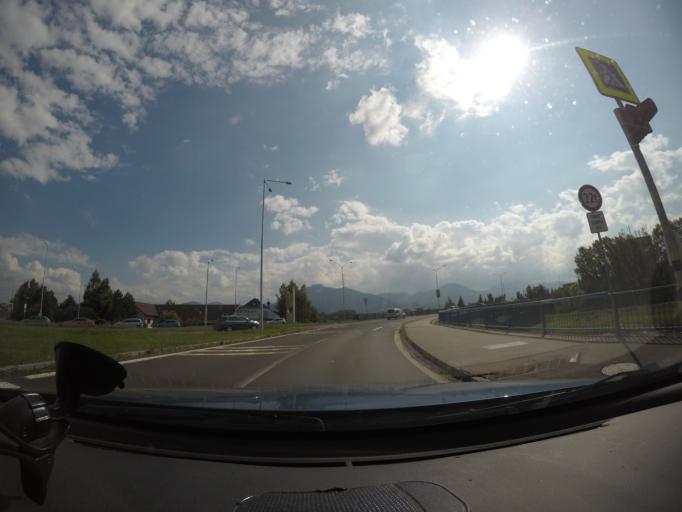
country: SK
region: Zilinsky
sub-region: Okres Liptovsky Mikulas
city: Liptovsky Mikulas
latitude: 49.0837
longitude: 19.6061
